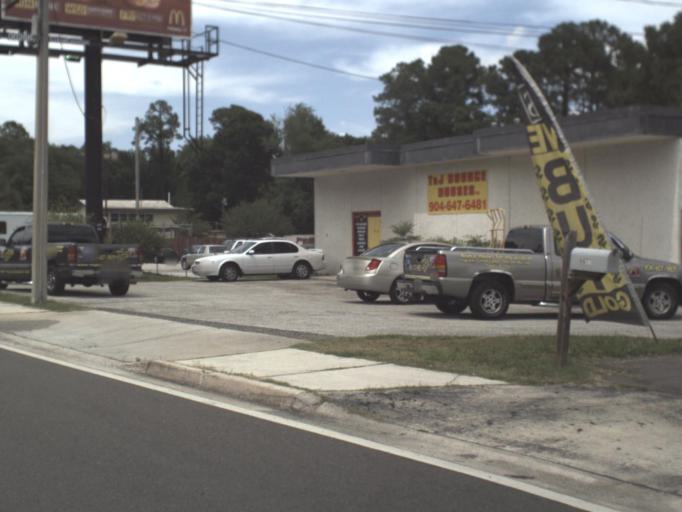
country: US
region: Florida
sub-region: Clay County
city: Bellair-Meadowbrook Terrace
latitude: 30.2275
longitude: -81.7381
